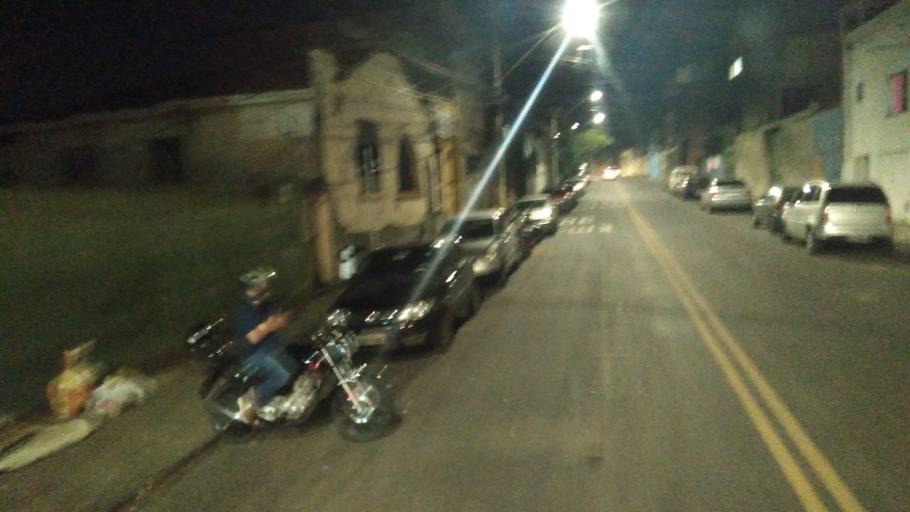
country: BR
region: Minas Gerais
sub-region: Belo Horizonte
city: Belo Horizonte
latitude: -19.9119
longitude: -43.9452
